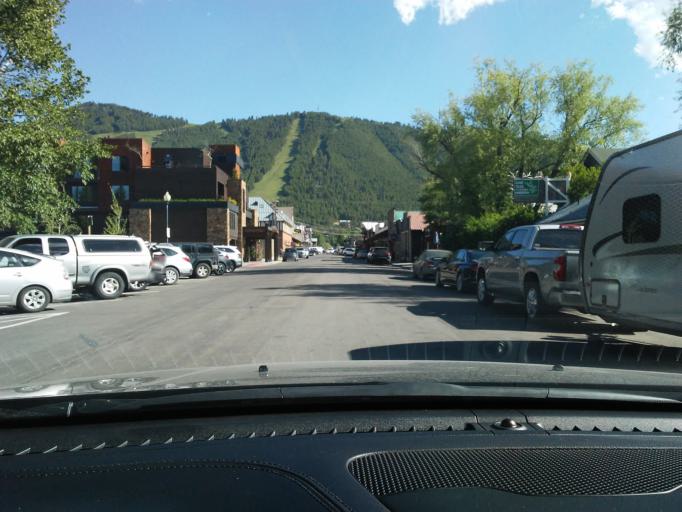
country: US
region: Wyoming
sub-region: Teton County
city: Jackson
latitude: 43.4812
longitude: -110.7636
